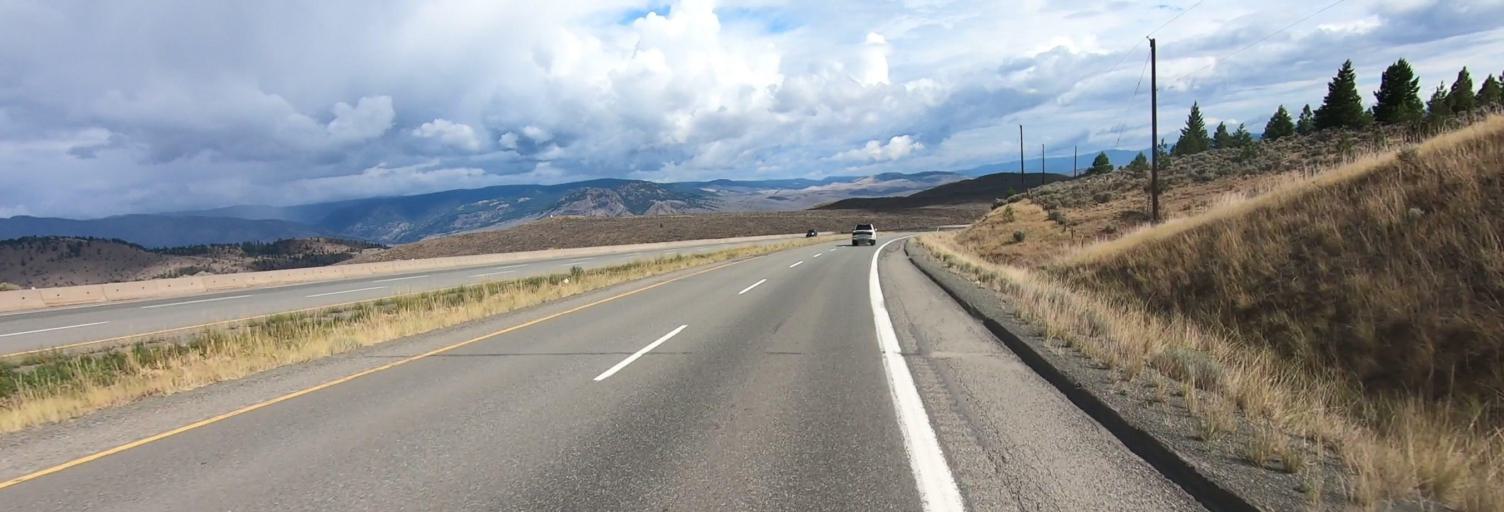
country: CA
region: British Columbia
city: Kamloops
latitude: 50.6504
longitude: -120.4841
